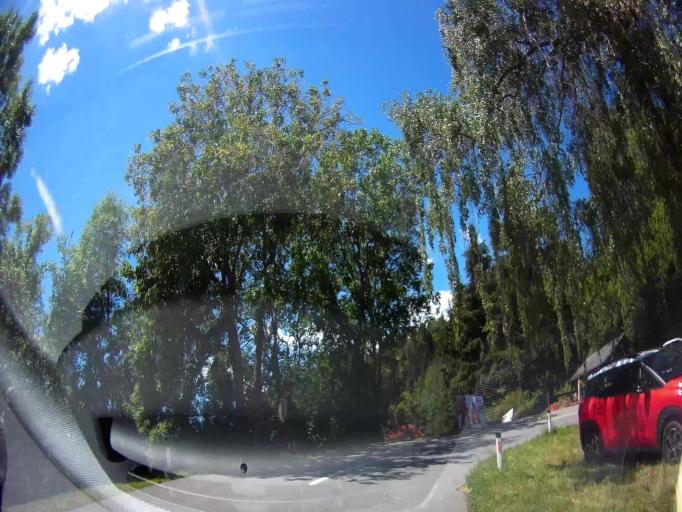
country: AT
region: Carinthia
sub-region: Politischer Bezirk Sankt Veit an der Glan
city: St. Georgen am Laengsee
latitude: 46.7240
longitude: 14.4311
